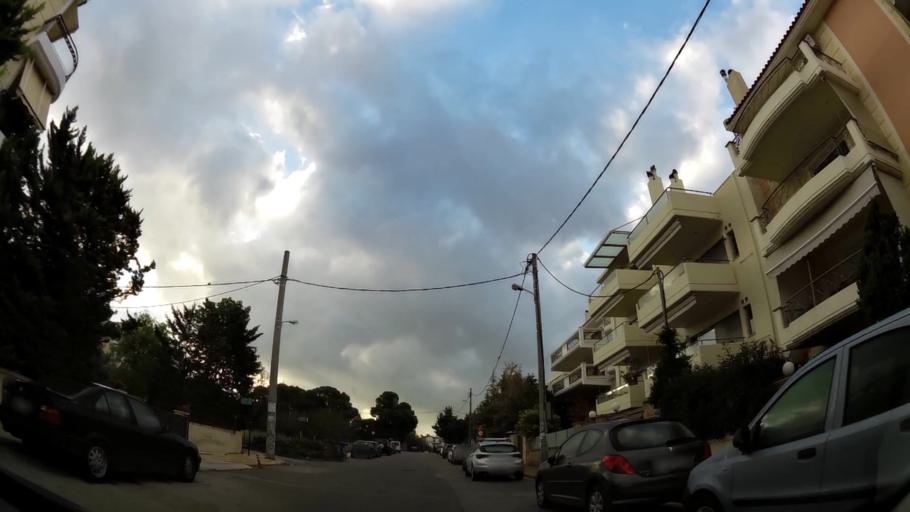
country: GR
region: Attica
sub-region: Nomarchia Athinas
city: Melissia
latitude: 38.0470
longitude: 23.8300
